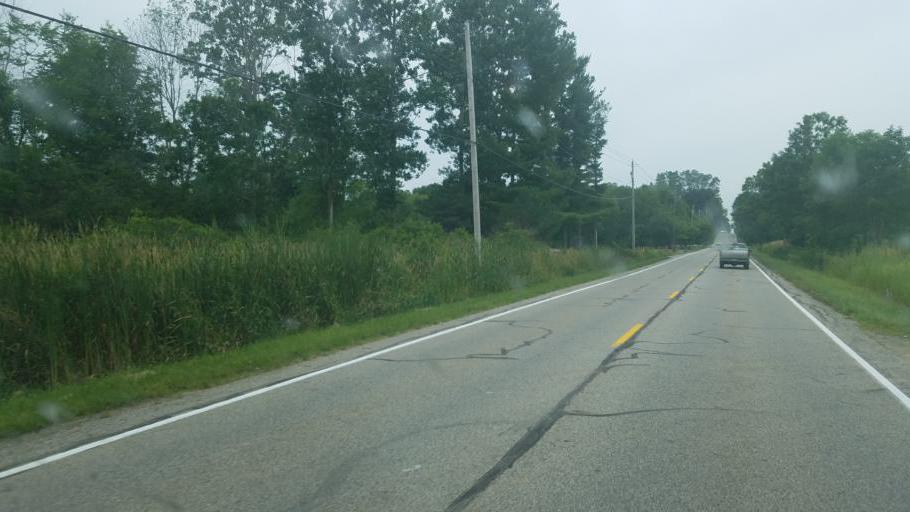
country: US
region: Ohio
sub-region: Portage County
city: Ravenna
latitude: 41.0999
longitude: -81.2760
